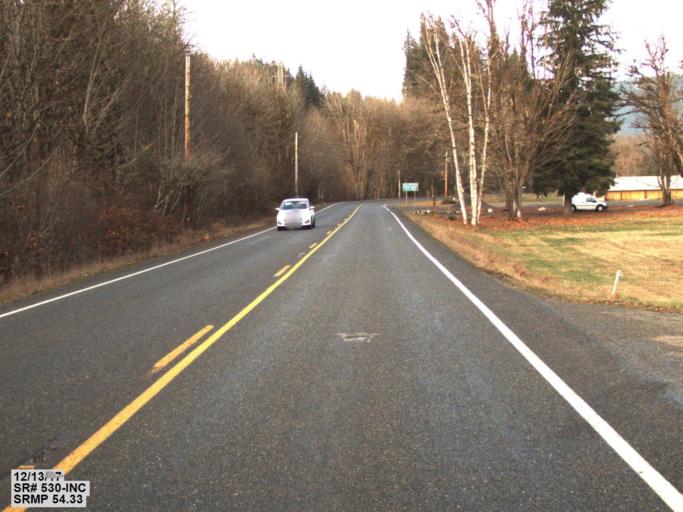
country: US
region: Washington
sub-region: Snohomish County
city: Darrington
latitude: 48.3190
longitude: -121.5549
